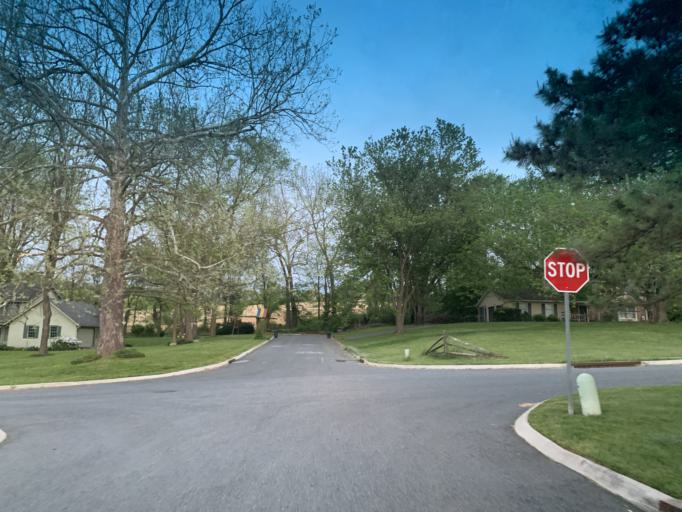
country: US
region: Maryland
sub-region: Harford County
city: South Bel Air
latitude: 39.5856
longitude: -76.2770
